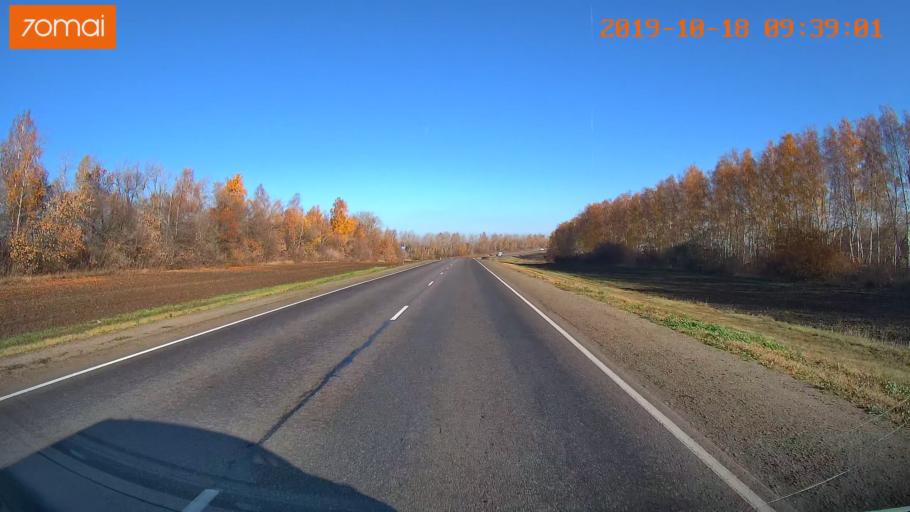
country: RU
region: Tula
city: Yefremov
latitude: 53.2469
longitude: 38.1347
